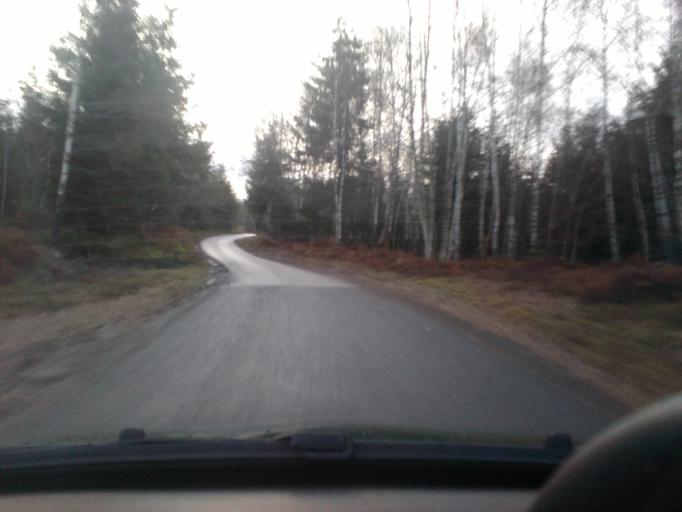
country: FR
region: Lorraine
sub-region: Departement des Vosges
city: Saint-Leonard
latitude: 48.2114
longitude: 6.9069
